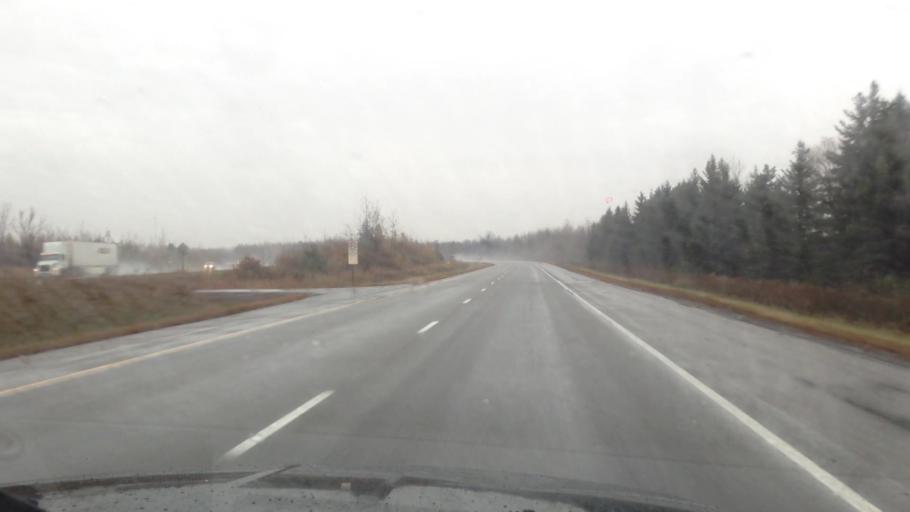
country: CA
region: Ontario
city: Casselman
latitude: 45.3084
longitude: -75.1497
